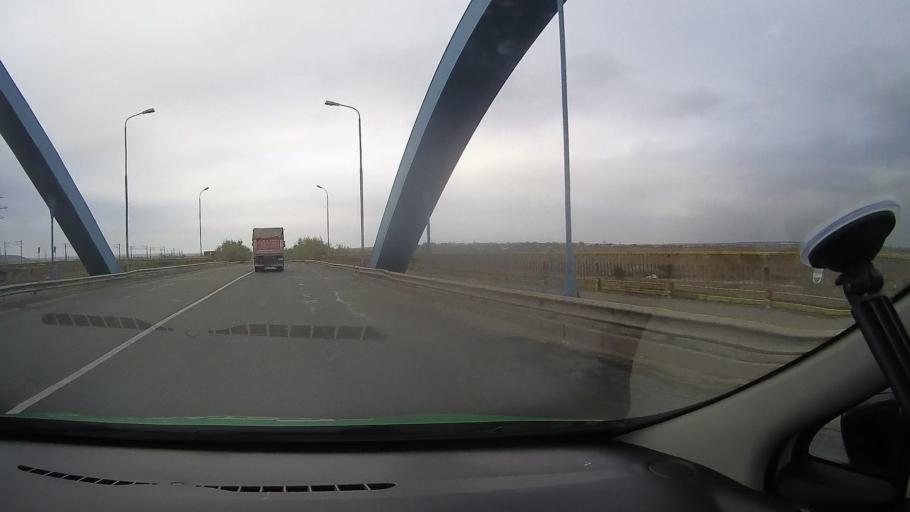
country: RO
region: Constanta
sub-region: Comuna Poarta Alba
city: Poarta Alba
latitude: 44.2178
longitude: 28.3891
